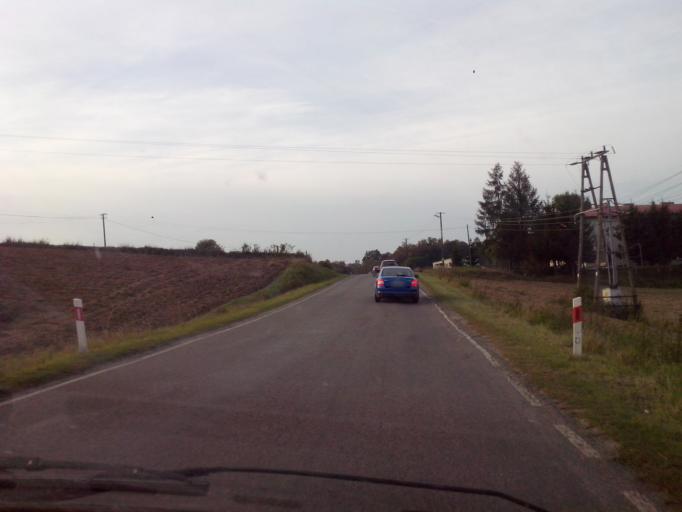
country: PL
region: Subcarpathian Voivodeship
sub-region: Powiat strzyzowski
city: Jawornik
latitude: 49.8135
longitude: 21.8431
